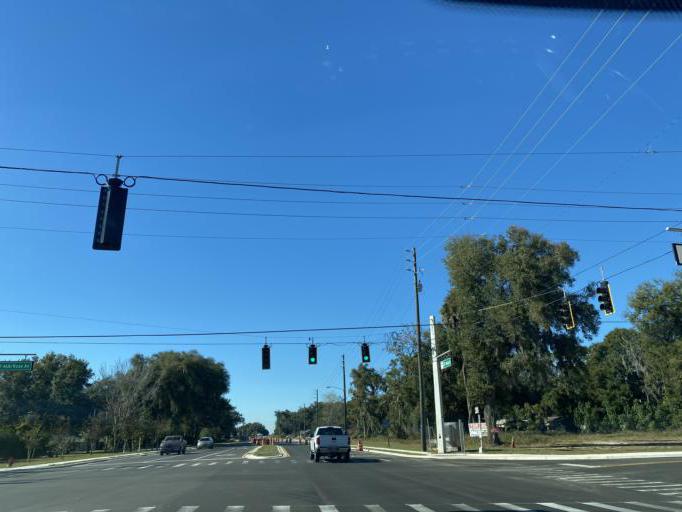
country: US
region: Florida
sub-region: Lake County
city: Fruitland Park
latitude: 28.8616
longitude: -81.9137
